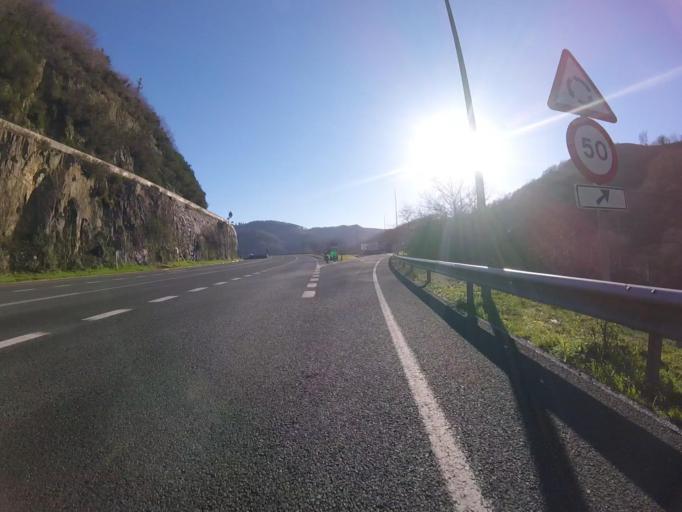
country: ES
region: Navarre
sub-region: Provincia de Navarra
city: Bera
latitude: 43.2839
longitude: -1.7121
